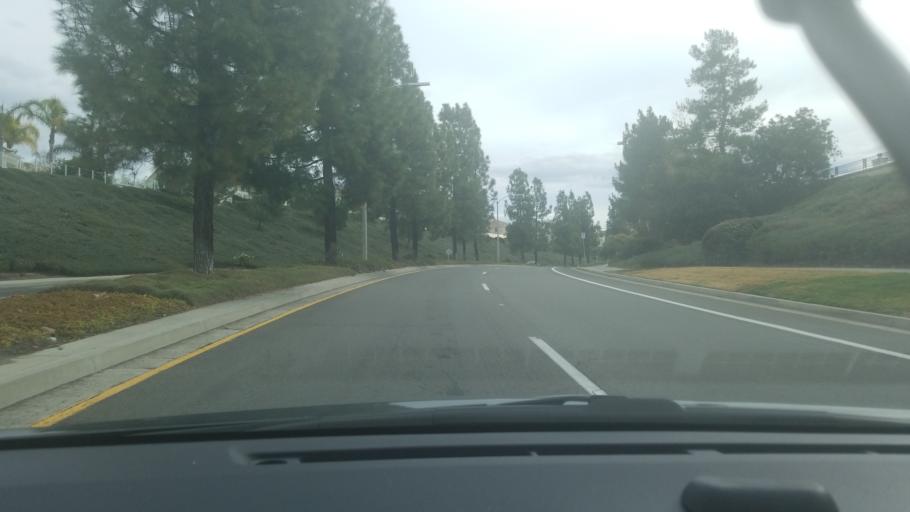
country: US
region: California
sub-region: Riverside County
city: Temecula
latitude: 33.4729
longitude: -117.0760
